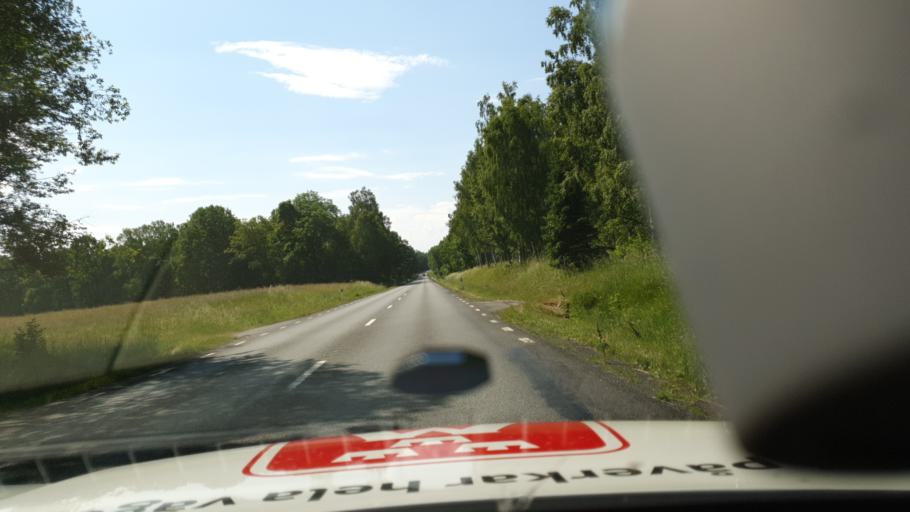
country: SE
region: Vaestra Goetaland
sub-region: Hjo Kommun
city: Hjo
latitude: 58.1075
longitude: 14.2083
